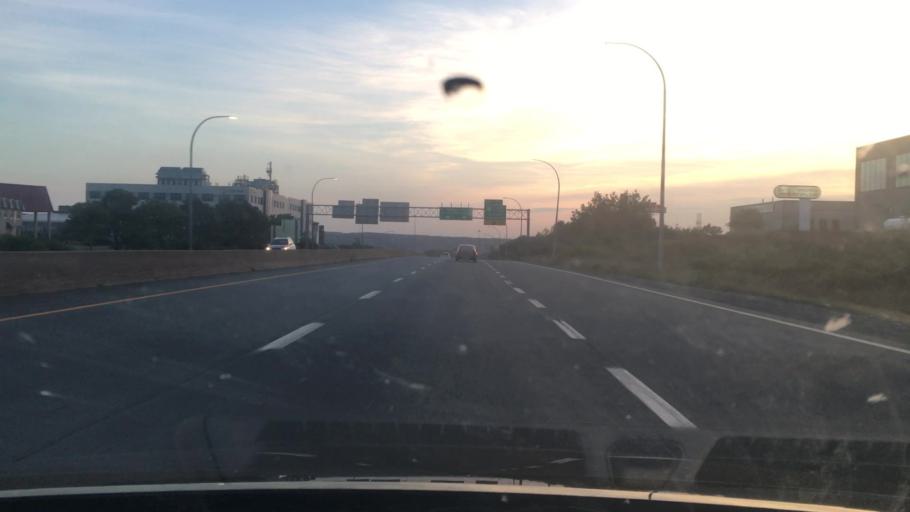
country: CA
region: Nova Scotia
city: Dartmouth
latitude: 44.6914
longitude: -63.5858
